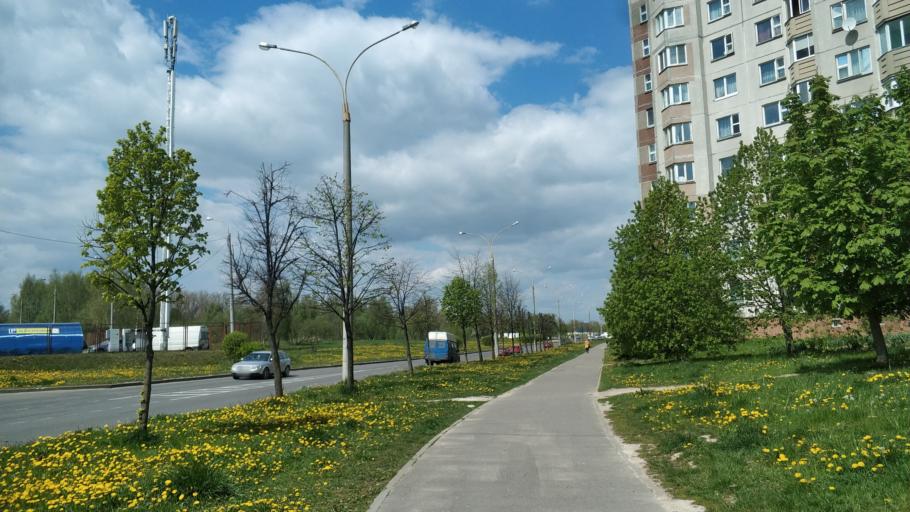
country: BY
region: Minsk
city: Syenitsa
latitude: 53.8360
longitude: 27.5679
